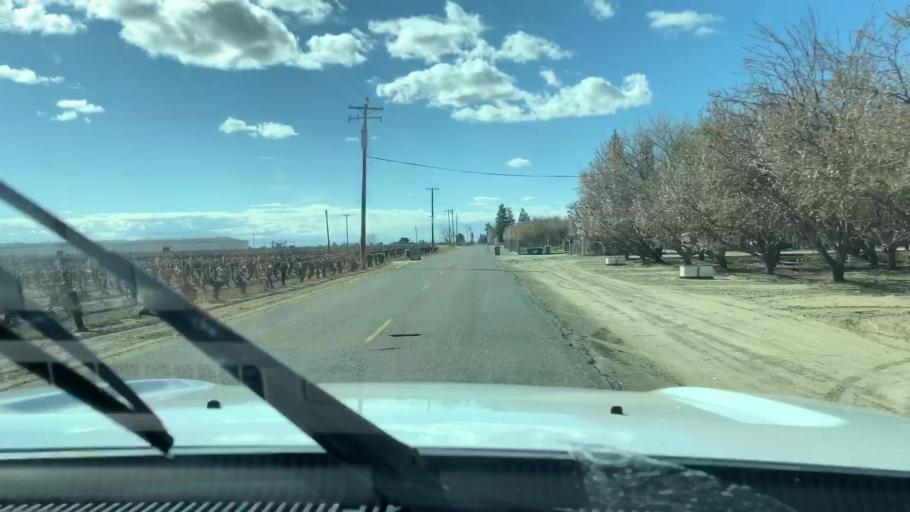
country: US
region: California
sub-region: Fresno County
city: Fowler
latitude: 36.5619
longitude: -119.7328
